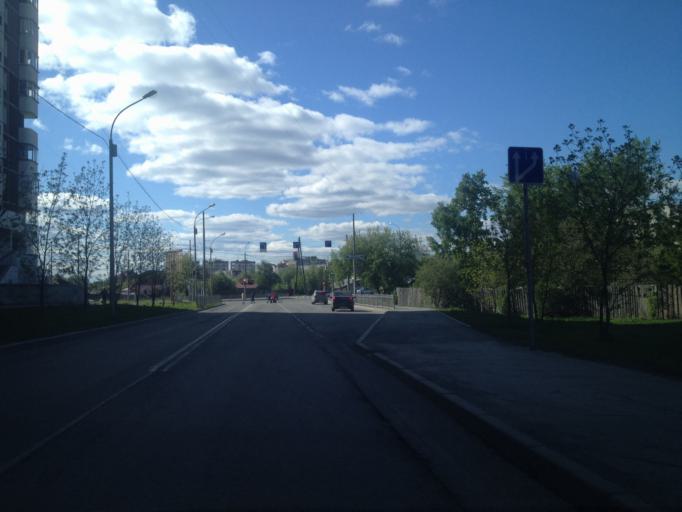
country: RU
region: Sverdlovsk
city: Sovkhoznyy
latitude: 56.8238
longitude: 60.5450
